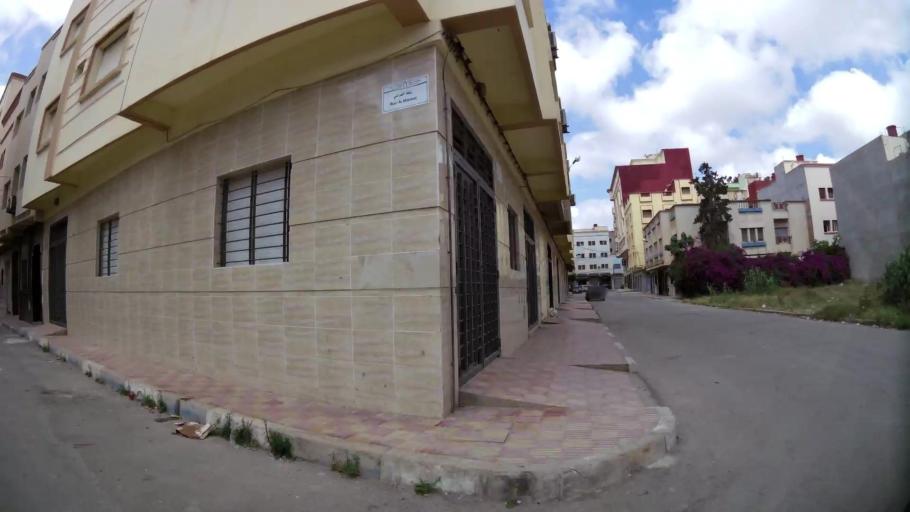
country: MA
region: Oriental
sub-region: Nador
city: Nador
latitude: 35.1619
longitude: -2.9273
